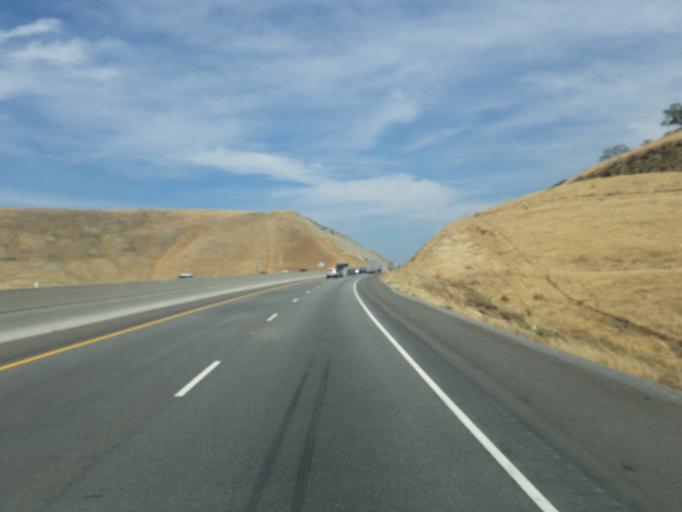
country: US
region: California
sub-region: Kern County
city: Bear Valley Springs
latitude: 35.2698
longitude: -118.6801
